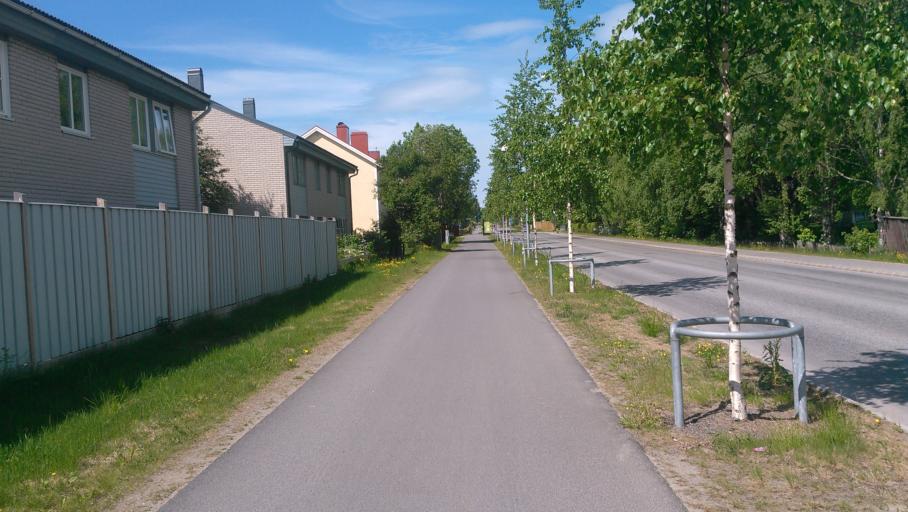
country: SE
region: Vaesterbotten
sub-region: Umea Kommun
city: Roback
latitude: 63.8348
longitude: 20.2013
